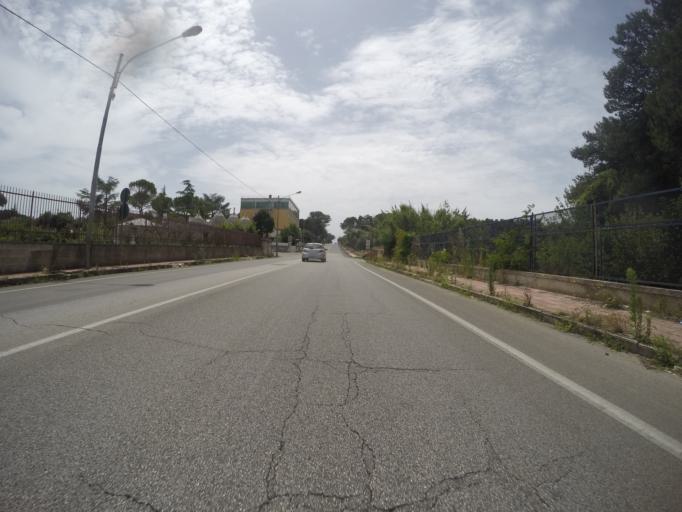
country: IT
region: Apulia
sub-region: Provincia di Taranto
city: Martina Franca
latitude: 40.6905
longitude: 17.3344
